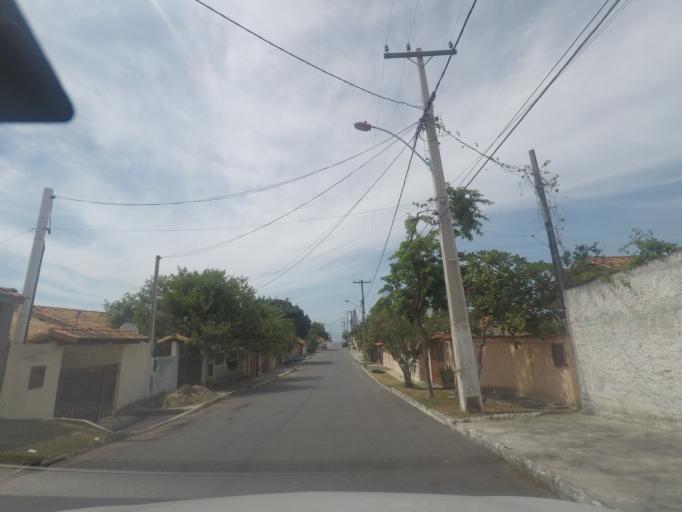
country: BR
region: Rio de Janeiro
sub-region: Marica
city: Marica
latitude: -22.9545
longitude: -42.7498
